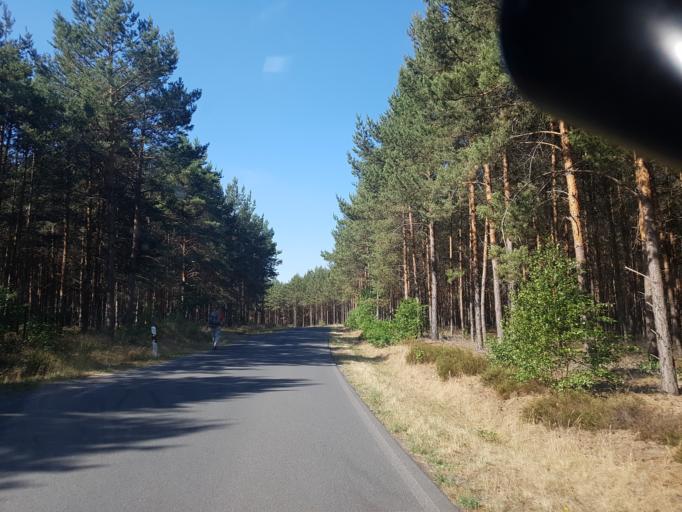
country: DE
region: Brandenburg
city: Treuenbrietzen
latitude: 52.0471
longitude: 12.8711
